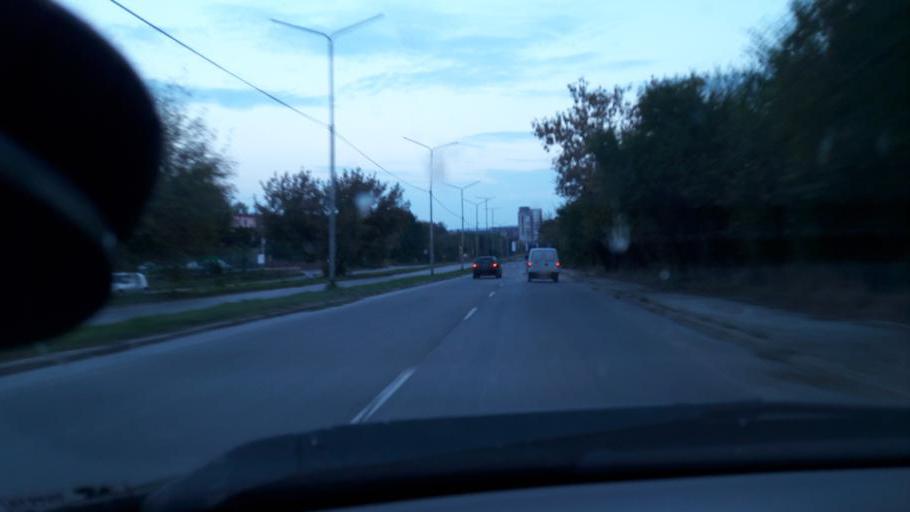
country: BG
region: Razgrad
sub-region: Obshtina Razgrad
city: Razgrad
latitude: 43.5386
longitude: 26.5183
